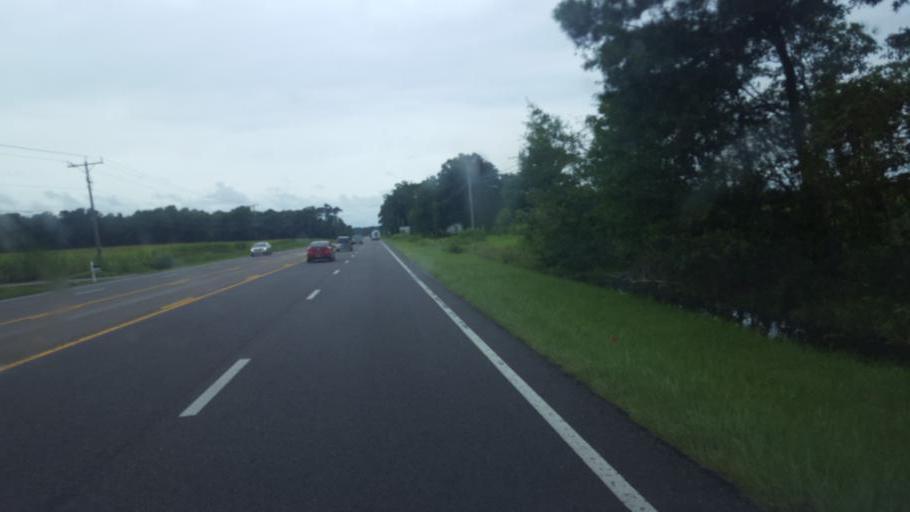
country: US
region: North Carolina
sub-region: Currituck County
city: Currituck
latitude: 36.2691
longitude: -75.9088
